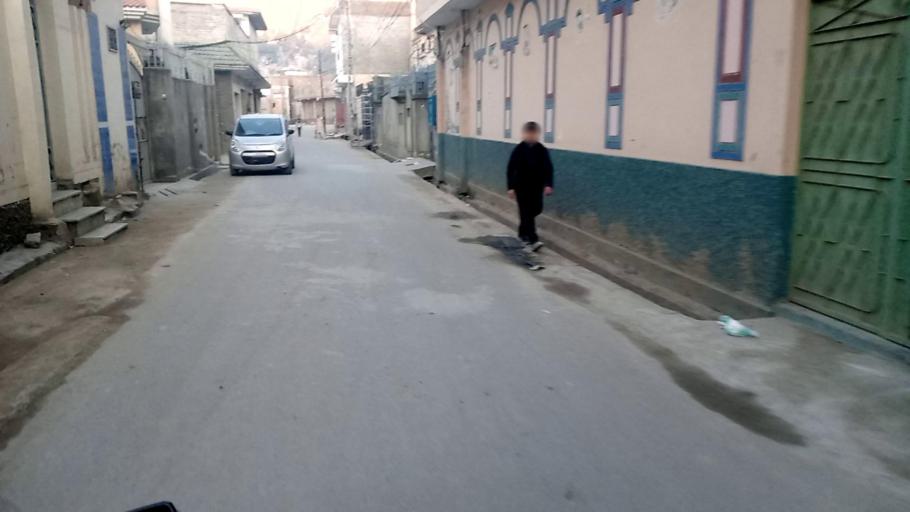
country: PK
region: Khyber Pakhtunkhwa
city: Saidu Sharif
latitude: 34.7470
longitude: 72.3504
